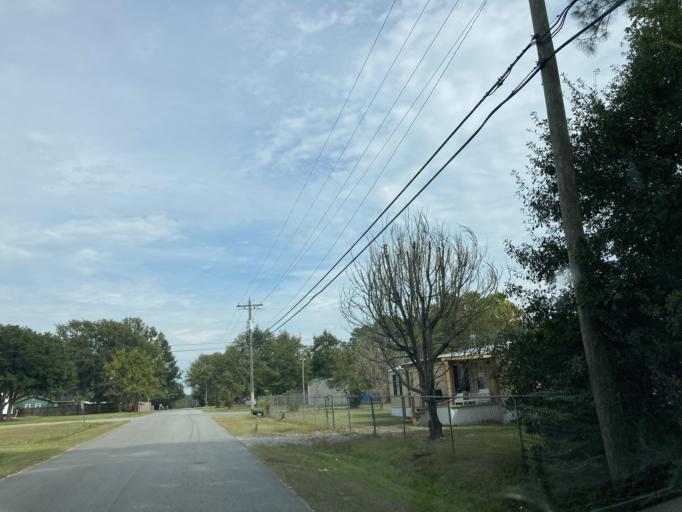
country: US
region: Mississippi
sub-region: Jackson County
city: Saint Martin
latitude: 30.4760
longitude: -88.8470
